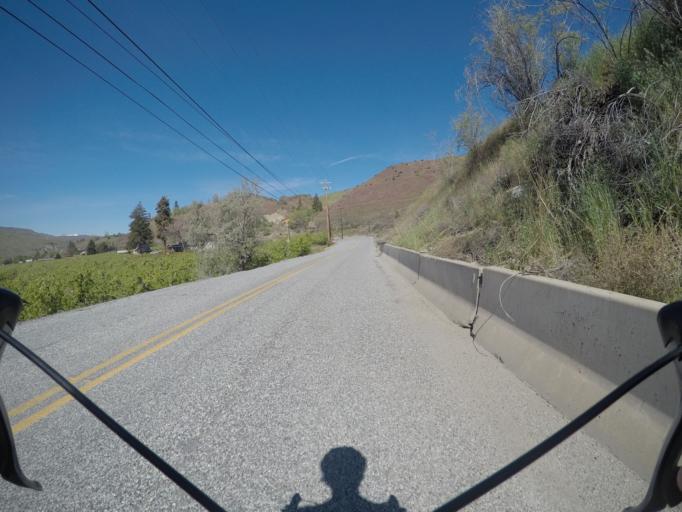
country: US
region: Washington
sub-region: Chelan County
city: Sunnyslope
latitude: 47.4701
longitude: -120.3531
